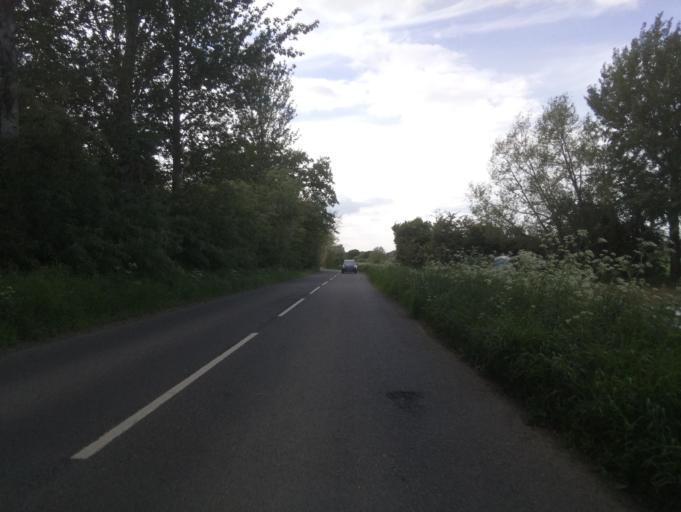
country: GB
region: England
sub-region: Gloucestershire
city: Chipping Campden
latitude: 52.0496
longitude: -1.7472
